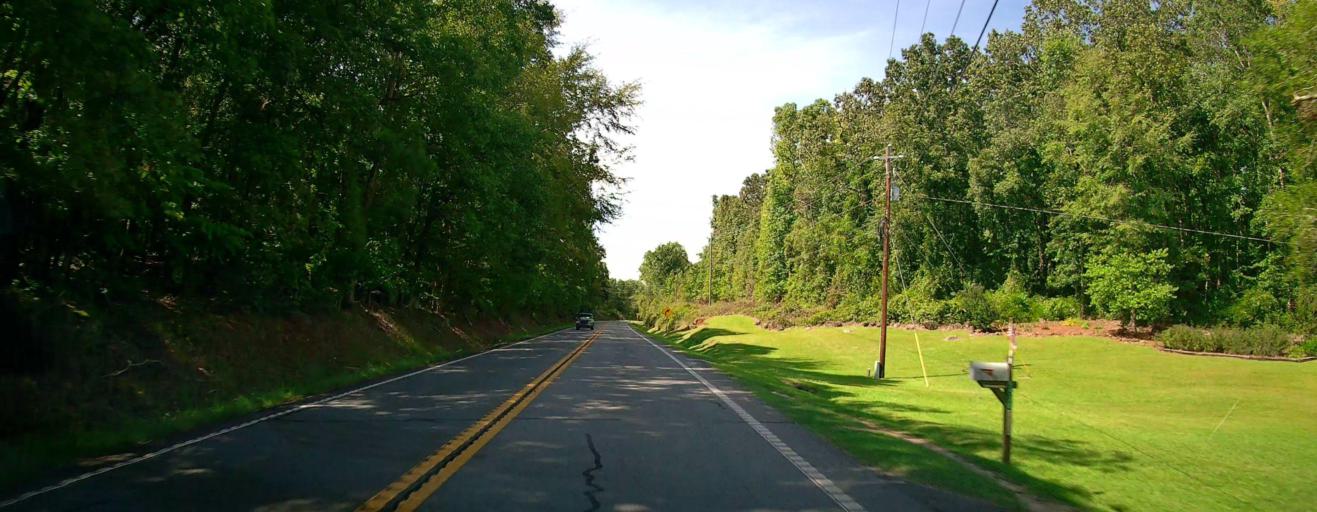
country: US
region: Georgia
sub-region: Talbot County
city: Talbotton
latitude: 32.7537
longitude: -84.5556
